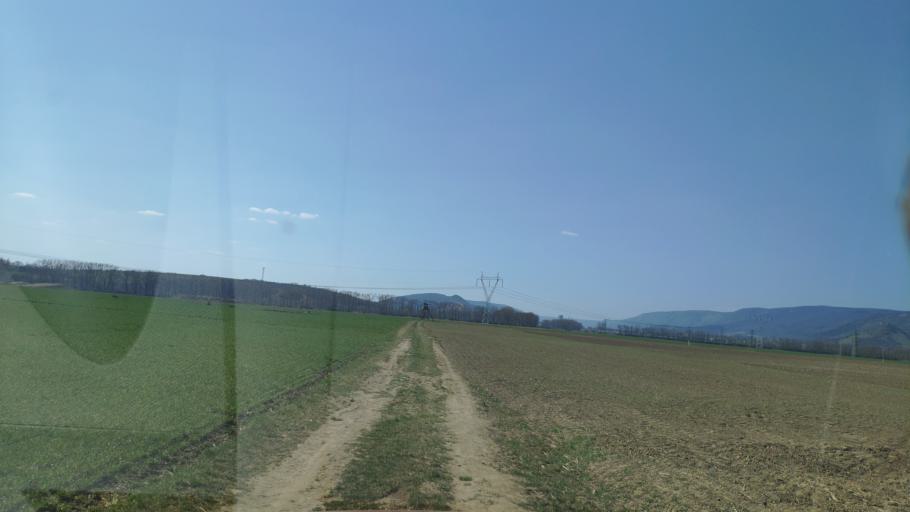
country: SK
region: Kosicky
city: Moldava nad Bodvou
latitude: 48.5957
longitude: 20.9365
